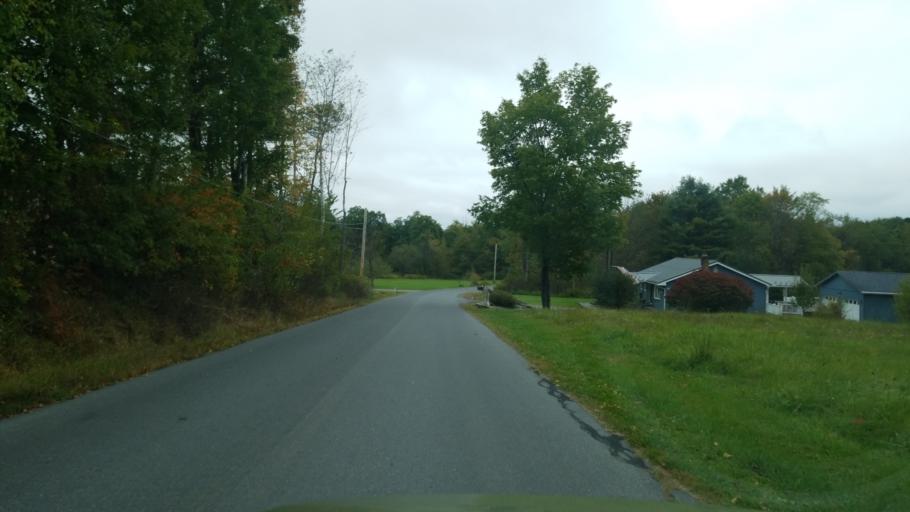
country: US
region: Pennsylvania
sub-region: Clearfield County
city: Curwensville
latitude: 41.0064
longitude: -78.5371
